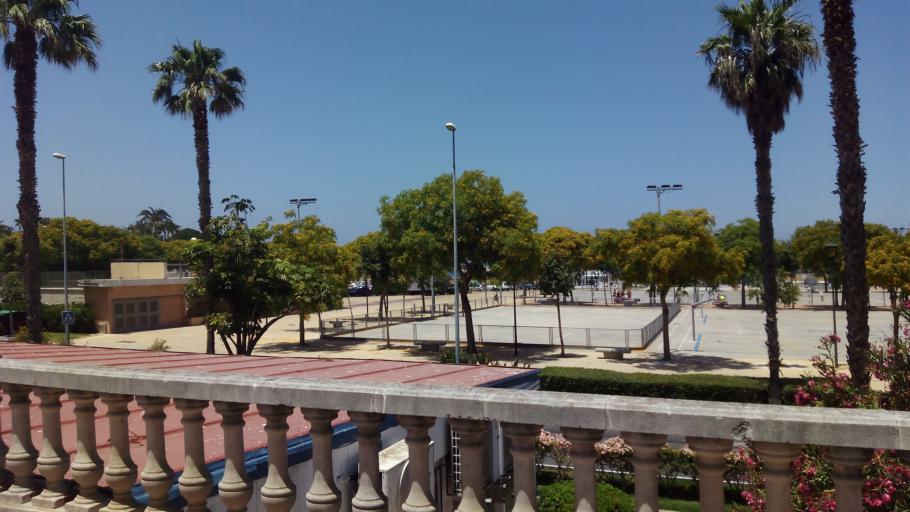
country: ES
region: Ceuta
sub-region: Ceuta
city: Ceuta
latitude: 35.8903
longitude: -5.3056
